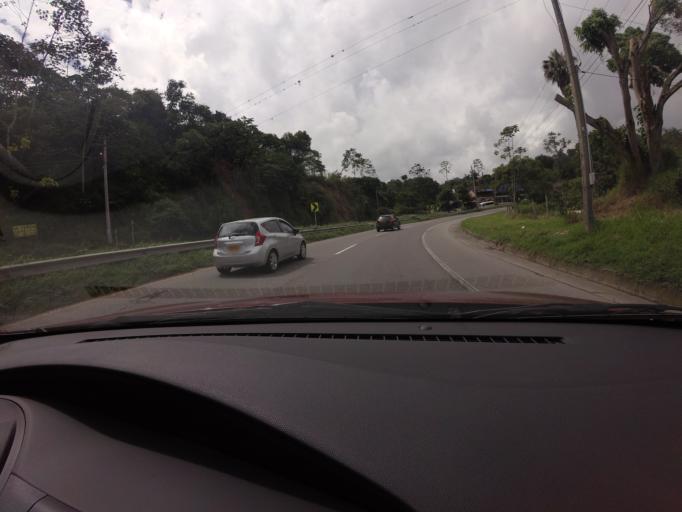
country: CO
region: Cundinamarca
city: Silvania
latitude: 4.3848
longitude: -74.3857
